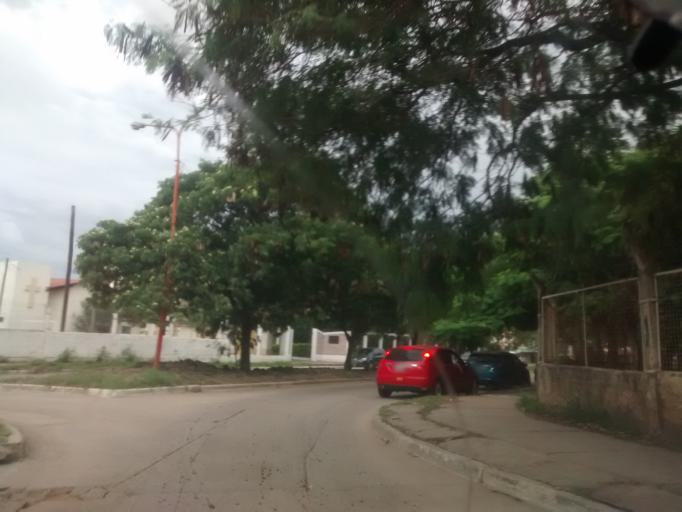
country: AR
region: Chaco
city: Fontana
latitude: -27.4431
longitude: -59.0166
